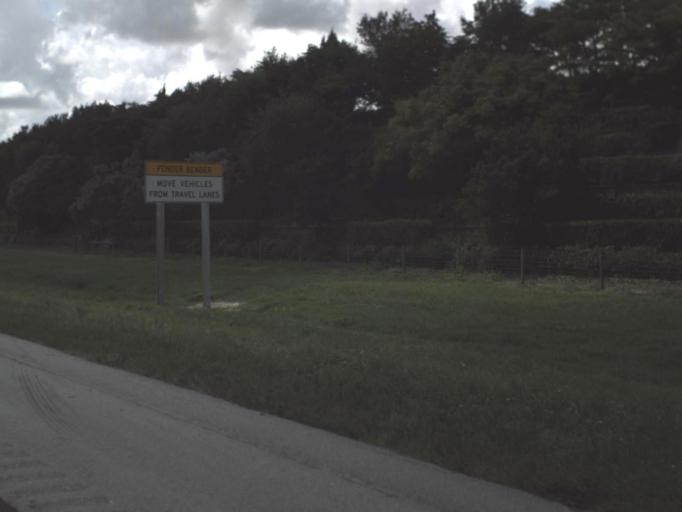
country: US
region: Florida
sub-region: Lee County
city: Bonita Springs
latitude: 26.3102
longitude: -81.7439
